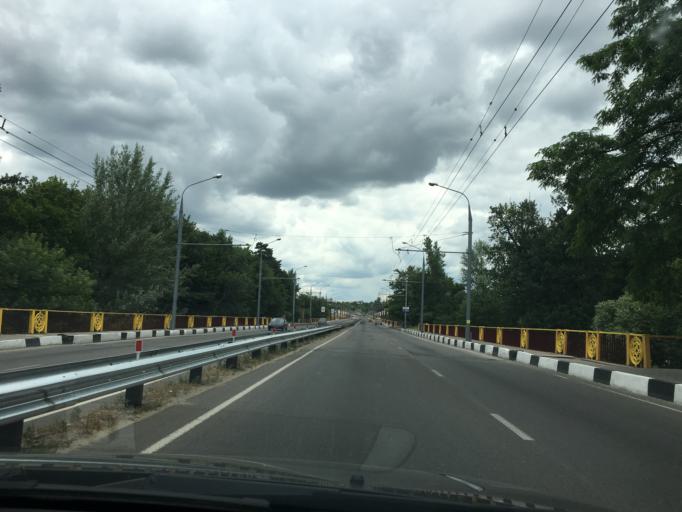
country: BY
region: Grodnenskaya
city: Hrodna
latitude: 53.6577
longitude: 23.8583
